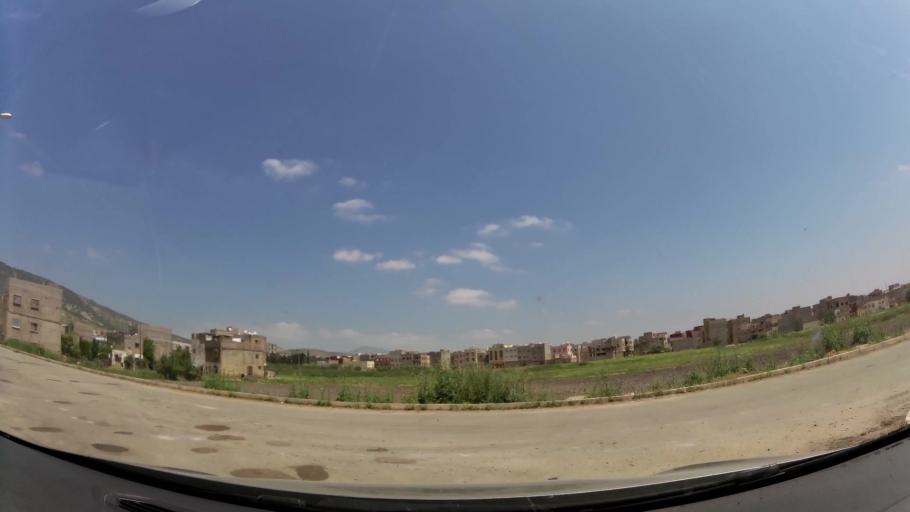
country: MA
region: Fes-Boulemane
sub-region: Fes
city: Fes
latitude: 34.0400
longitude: -5.0548
